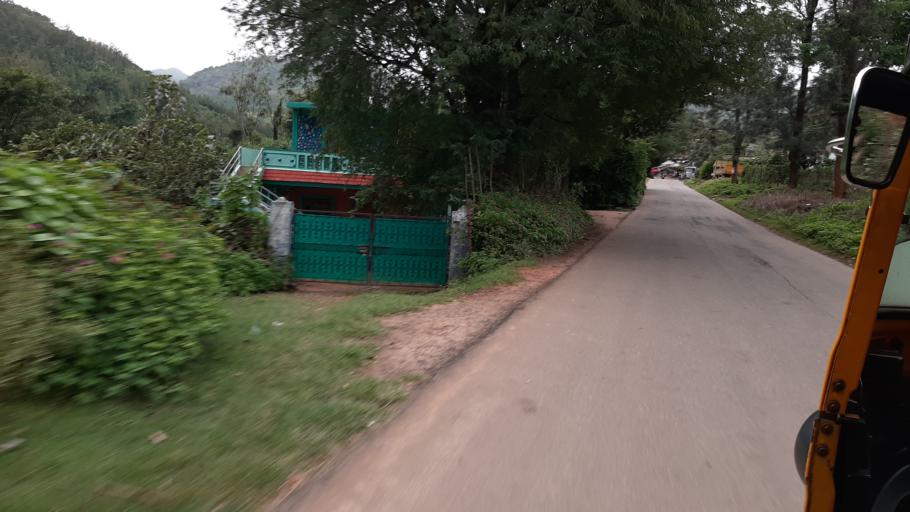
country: IN
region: Andhra Pradesh
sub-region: Vizianagaram District
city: Salur
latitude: 18.2379
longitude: 83.0023
